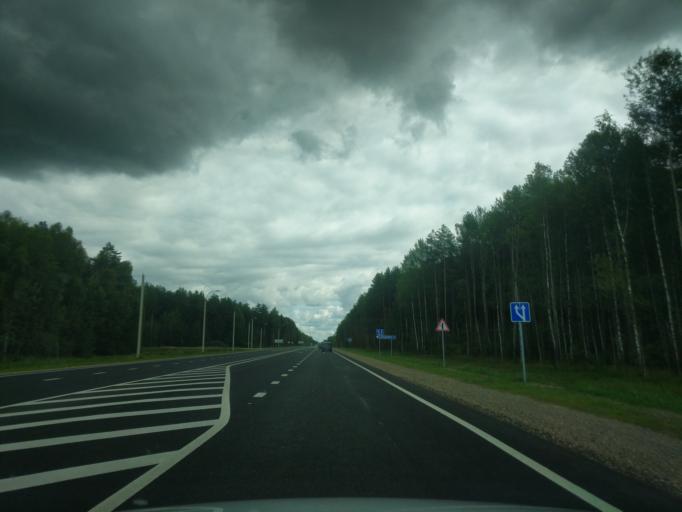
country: RU
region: Jaroslavl
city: Tunoshna
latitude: 57.5473
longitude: 40.1635
